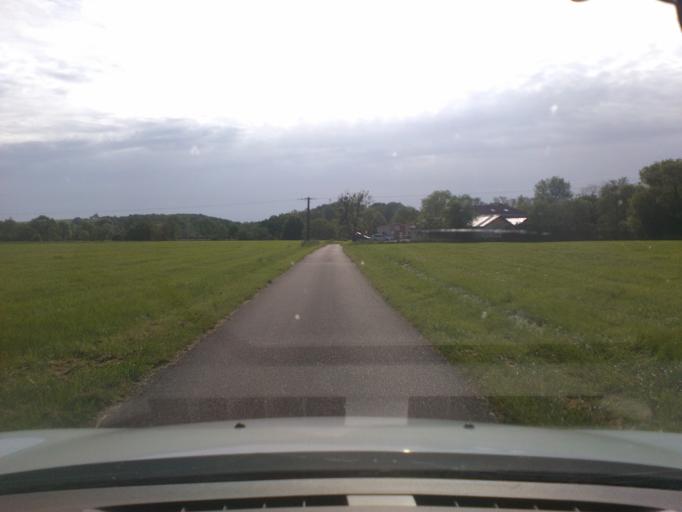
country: FR
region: Lorraine
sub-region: Departement des Vosges
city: Mirecourt
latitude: 48.3497
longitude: 6.1562
